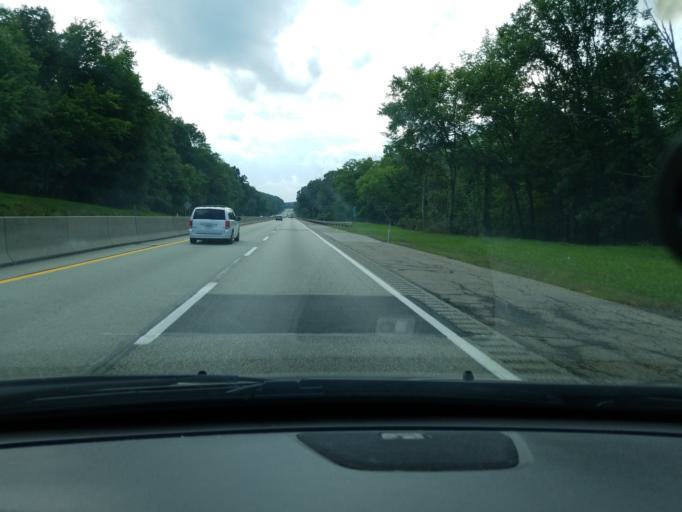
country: US
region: Pennsylvania
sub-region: Lawrence County
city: Ellport
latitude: 40.7863
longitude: -80.2483
